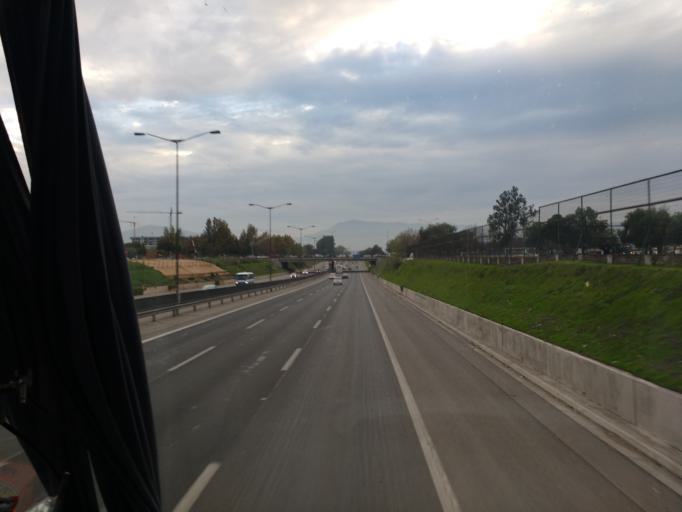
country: CL
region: Santiago Metropolitan
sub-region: Provincia de Santiago
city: Lo Prado
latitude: -33.4539
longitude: -70.7363
